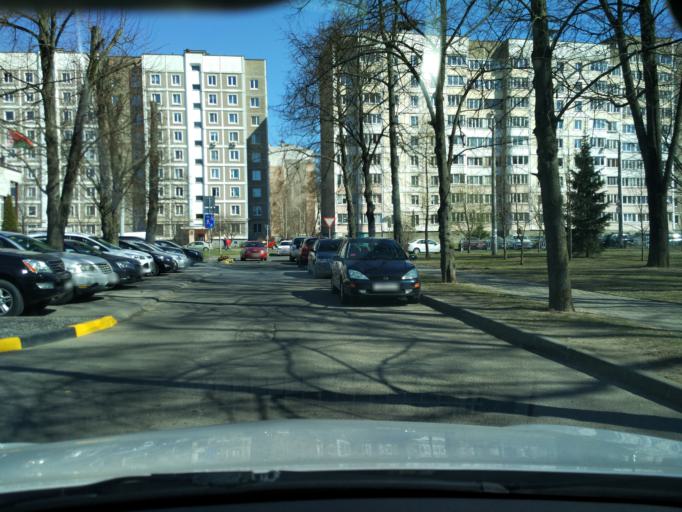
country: BY
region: Minsk
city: Minsk
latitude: 53.8790
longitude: 27.5554
